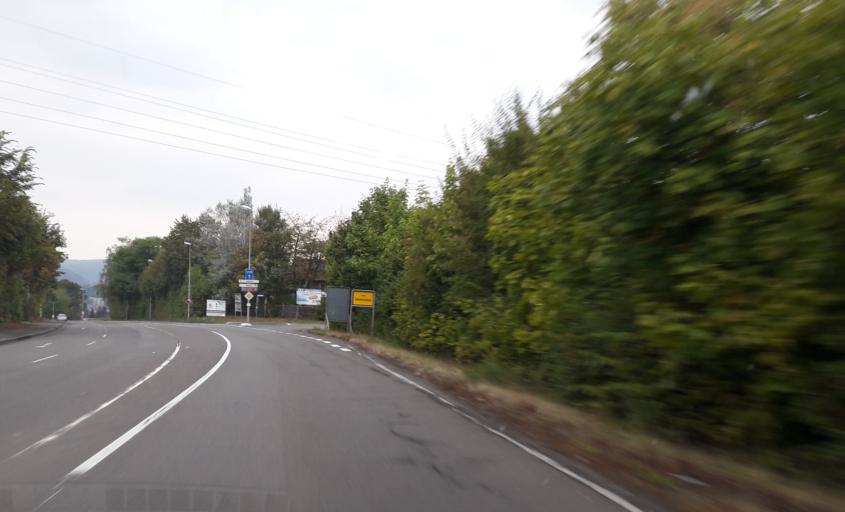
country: DE
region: Rheinland-Pfalz
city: Zweibrucken
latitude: 49.2426
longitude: 7.3886
